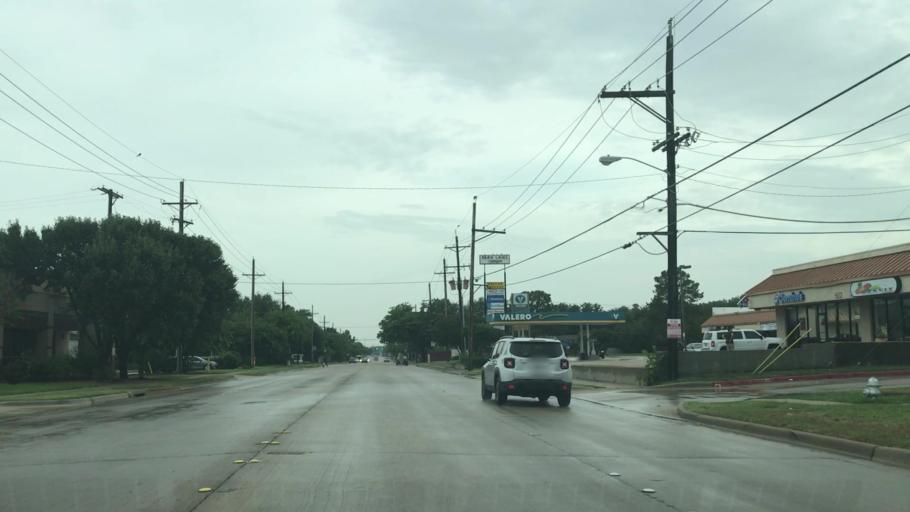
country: US
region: Texas
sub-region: Denton County
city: Lewisville
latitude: 33.0407
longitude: -97.0275
